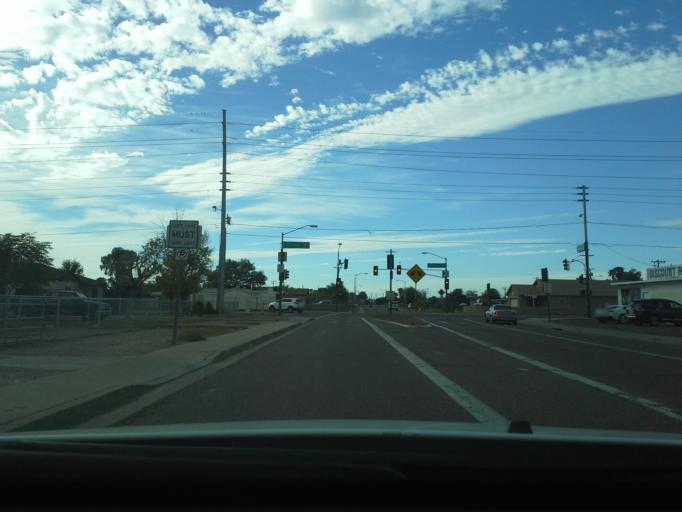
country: US
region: Arizona
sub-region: Maricopa County
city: Phoenix
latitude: 33.4491
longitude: -112.1167
